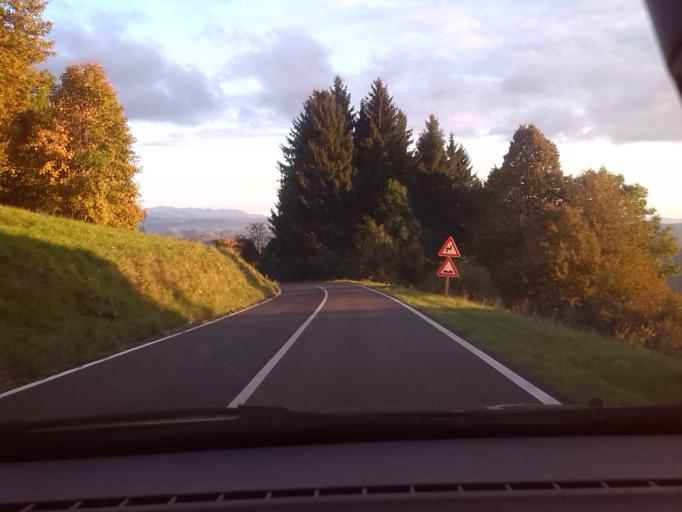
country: IT
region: Friuli Venezia Giulia
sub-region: Provincia di Udine
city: Savogna
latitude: 46.1940
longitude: 13.5338
